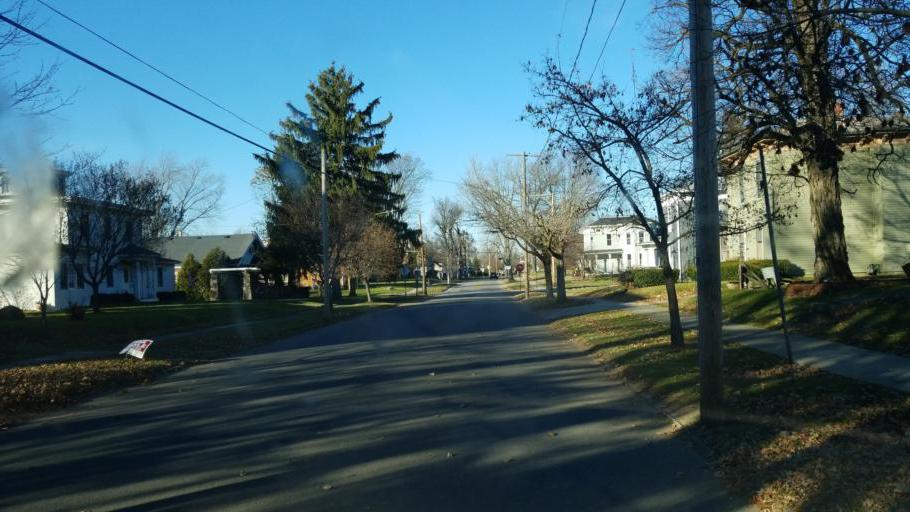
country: US
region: Ohio
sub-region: Morrow County
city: Cardington
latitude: 40.4958
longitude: -82.8939
